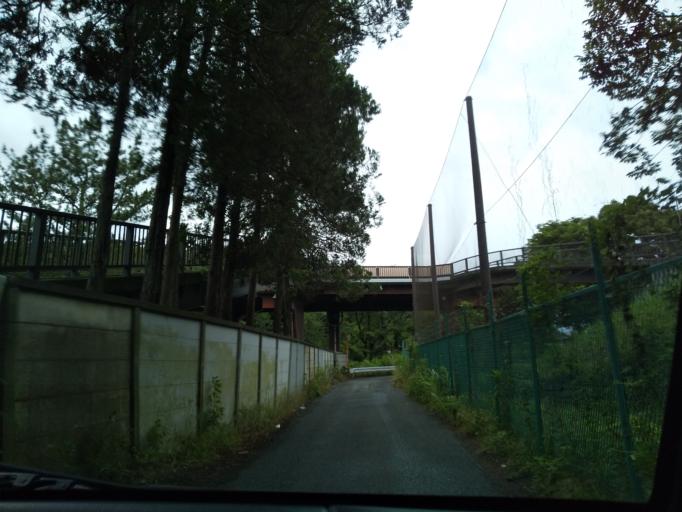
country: JP
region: Kanagawa
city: Minami-rinkan
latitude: 35.4271
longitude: 139.4433
